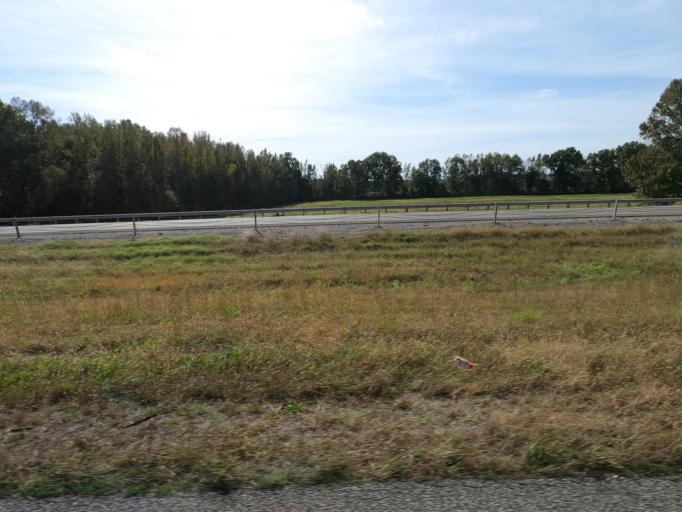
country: US
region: Tennessee
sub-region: Humphreys County
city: New Johnsonville
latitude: 35.8819
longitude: -87.8225
